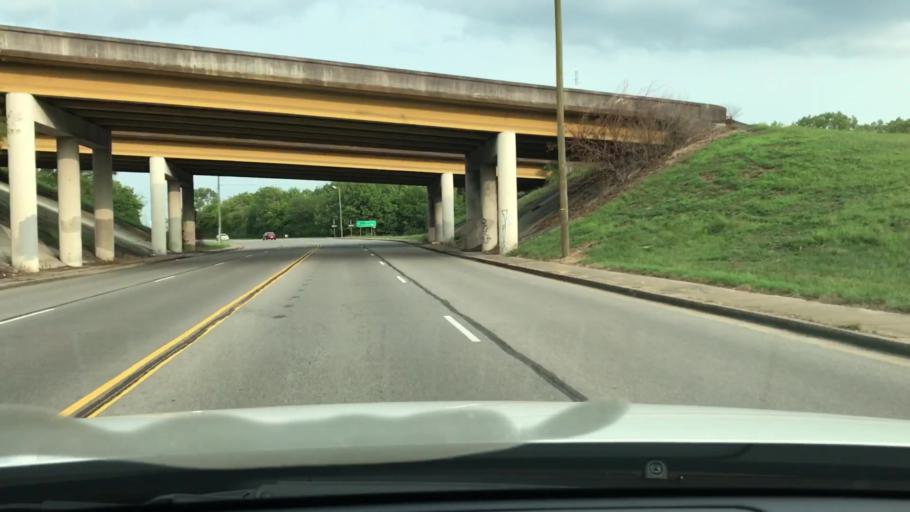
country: US
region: Tennessee
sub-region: Davidson County
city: Nashville
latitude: 36.2185
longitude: -86.7480
